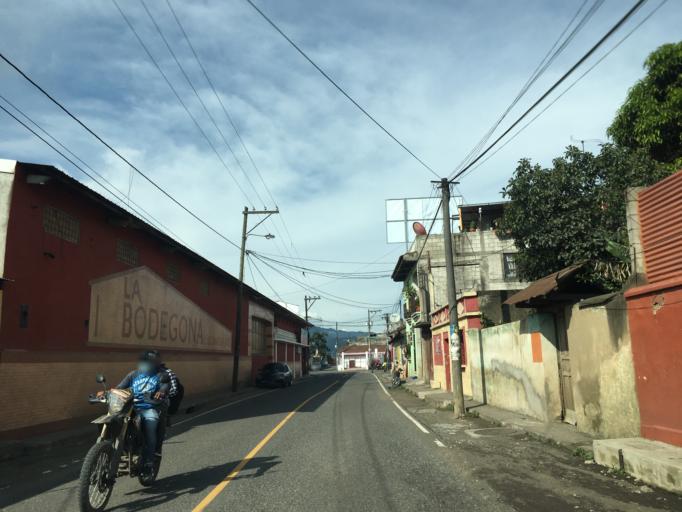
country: GT
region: Sacatepequez
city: Ciudad Vieja
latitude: 14.5234
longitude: -90.7685
